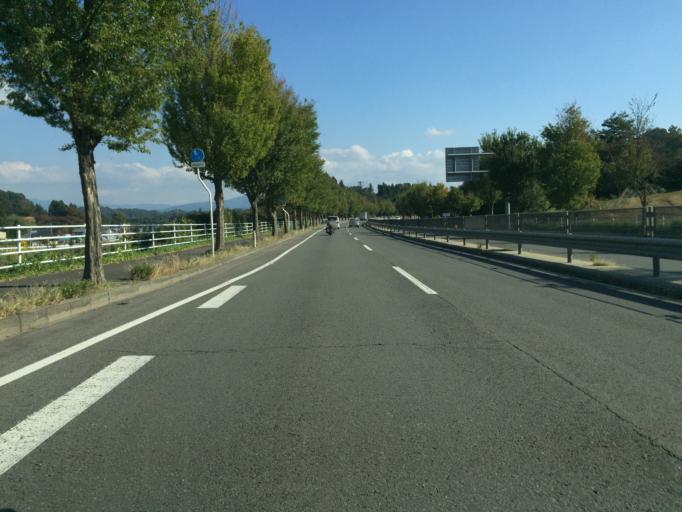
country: JP
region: Fukushima
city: Fukushima-shi
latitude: 37.6696
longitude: 140.4840
